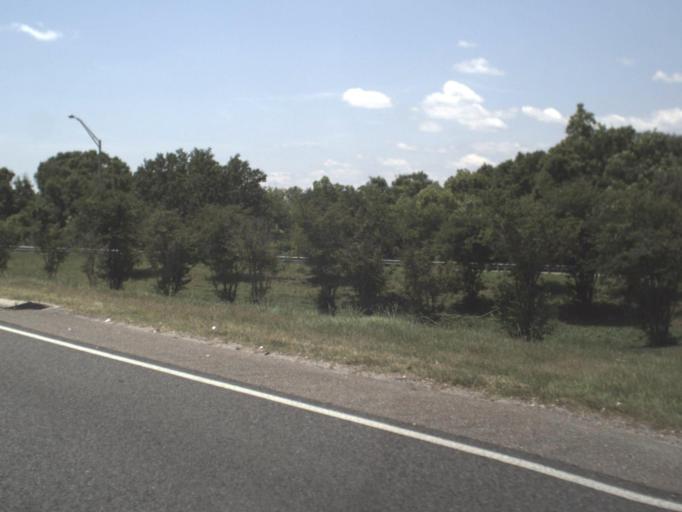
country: US
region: Florida
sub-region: Duval County
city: Jacksonville
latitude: 30.3551
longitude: -81.6687
